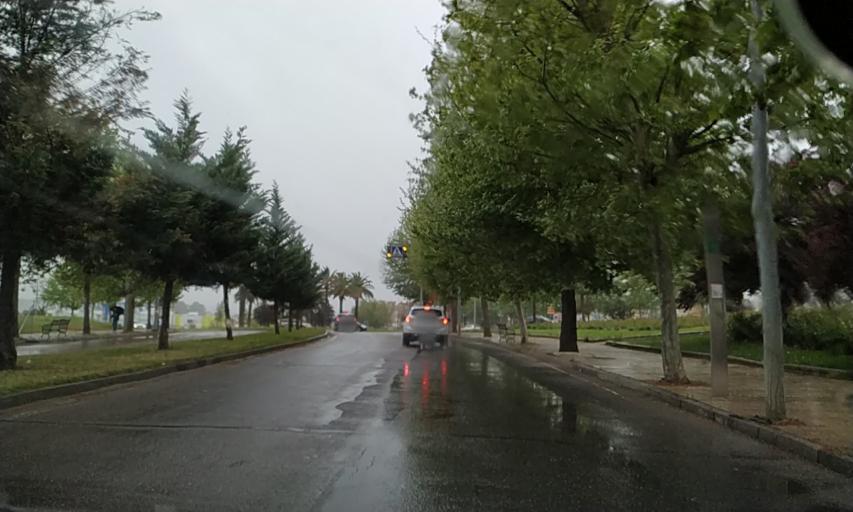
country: ES
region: Extremadura
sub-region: Provincia de Badajoz
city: Badajoz
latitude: 38.8629
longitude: -6.9726
